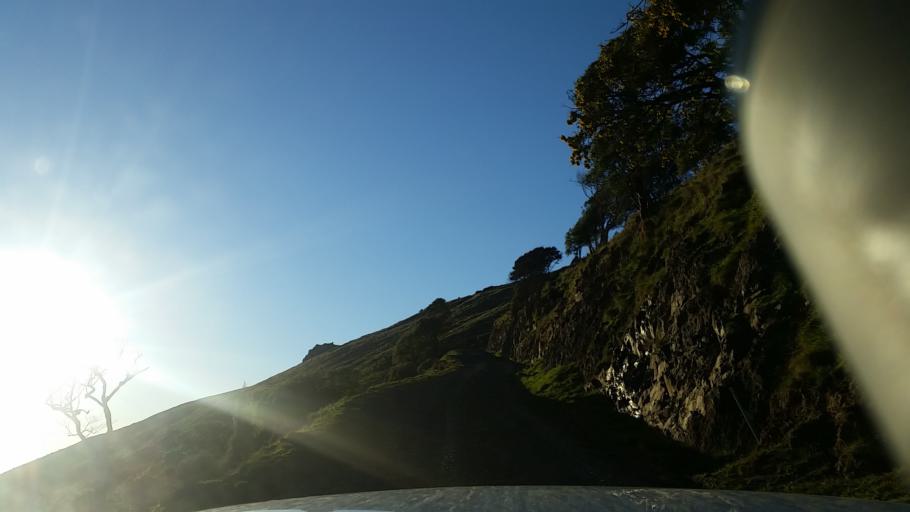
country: NZ
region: Canterbury
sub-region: Christchurch City
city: Christchurch
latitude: -43.7239
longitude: 173.0987
